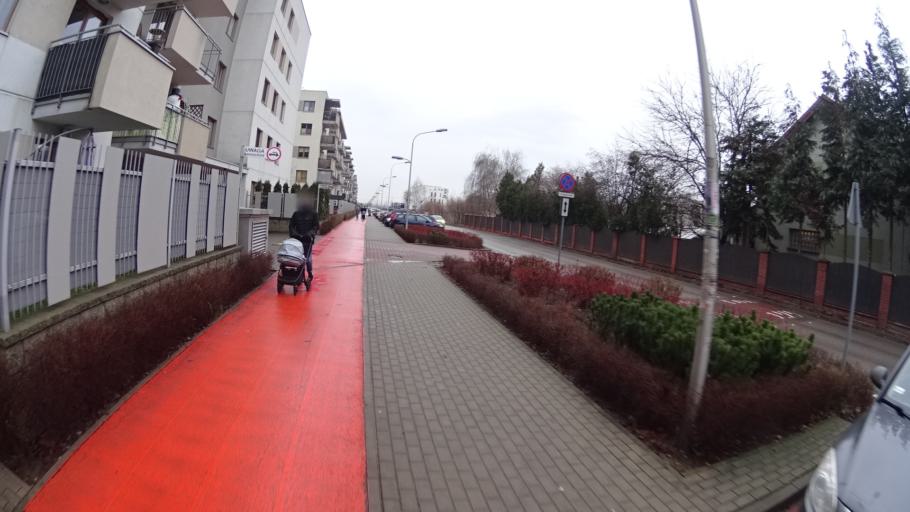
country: PL
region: Masovian Voivodeship
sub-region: Warszawa
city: Bemowo
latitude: 52.2315
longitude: 20.8916
